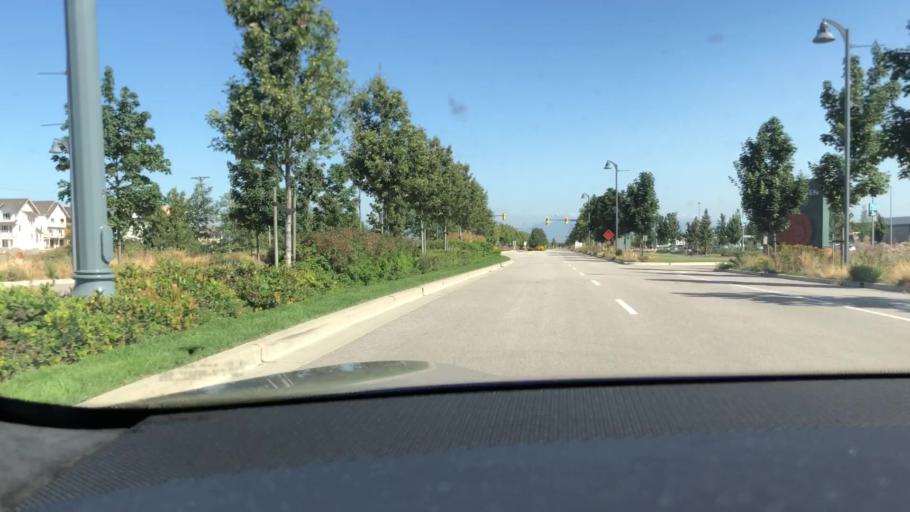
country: US
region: Washington
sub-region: Whatcom County
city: Point Roberts
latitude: 49.0335
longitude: -123.0903
